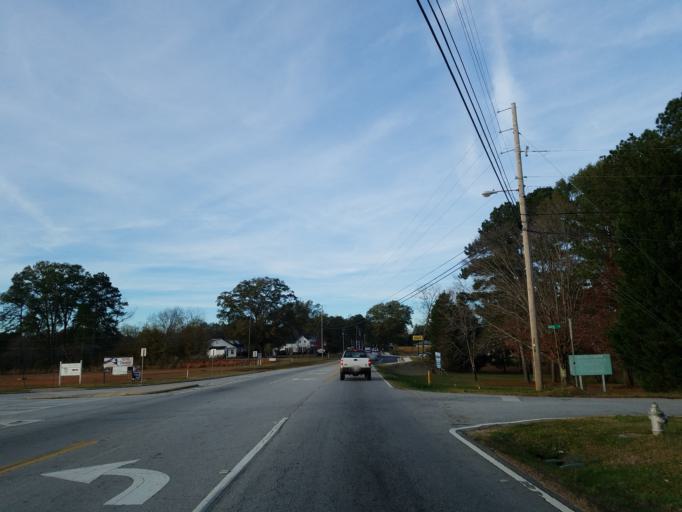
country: US
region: Georgia
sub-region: Carroll County
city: Temple
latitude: 33.7282
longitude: -85.0285
